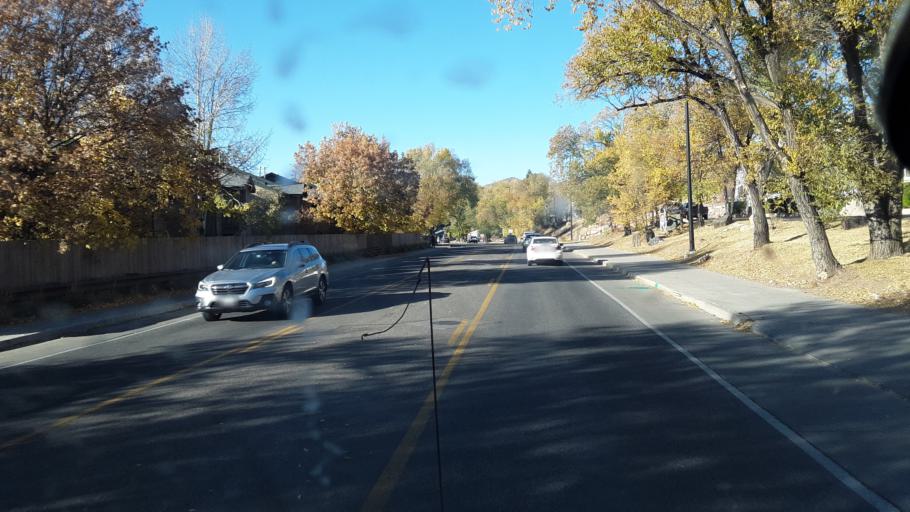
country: US
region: Colorado
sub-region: La Plata County
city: Durango
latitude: 37.2956
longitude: -107.8551
